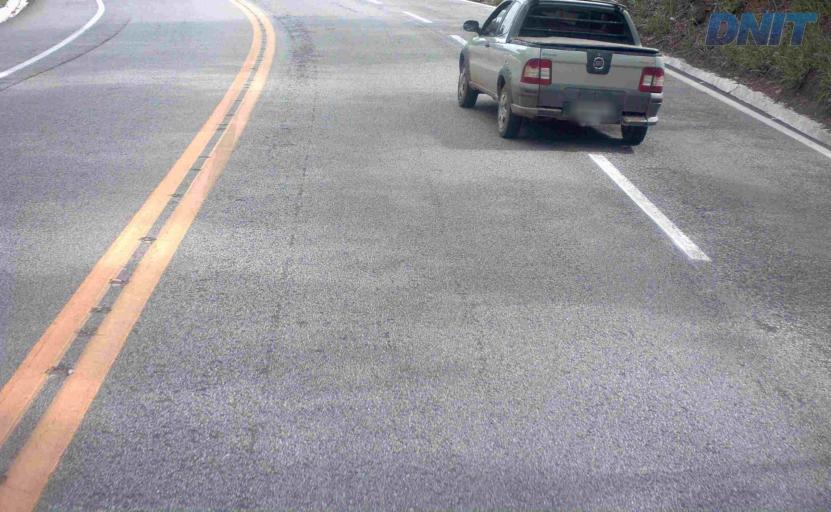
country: BR
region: Minas Gerais
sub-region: Caete
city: Caete
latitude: -19.7370
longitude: -43.6022
